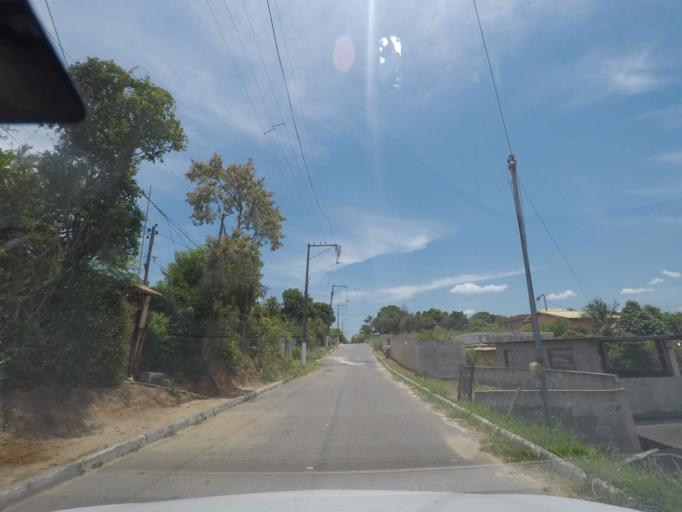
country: BR
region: Rio de Janeiro
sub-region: Marica
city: Marica
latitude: -22.9301
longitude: -42.8248
